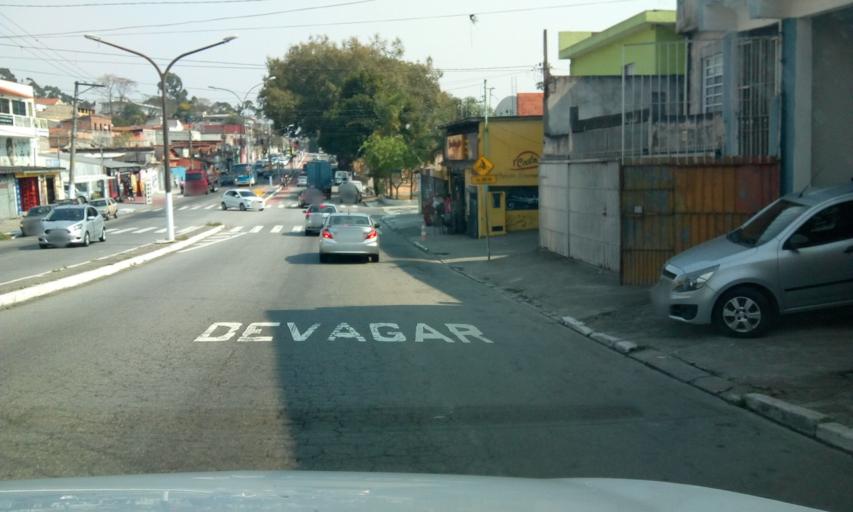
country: BR
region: Sao Paulo
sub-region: Diadema
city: Diadema
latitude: -23.7139
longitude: -46.6897
